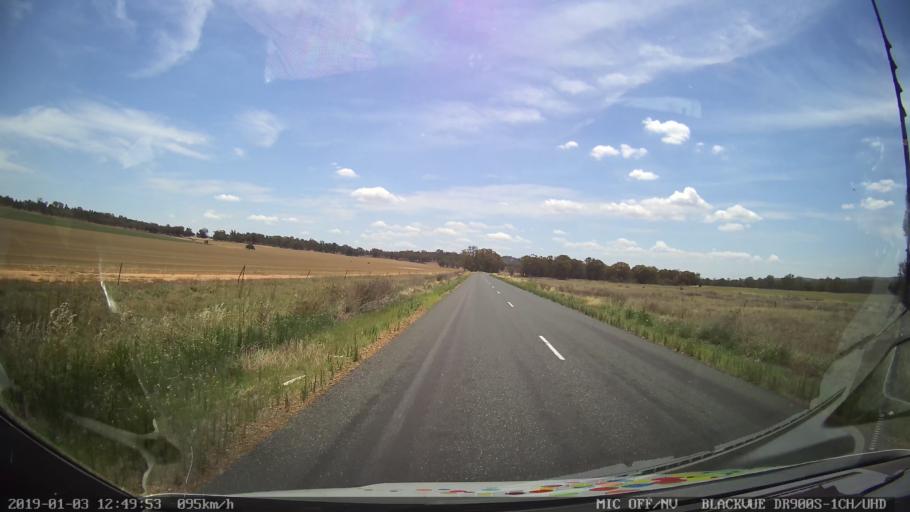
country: AU
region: New South Wales
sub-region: Weddin
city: Grenfell
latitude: -33.6978
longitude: 148.2647
